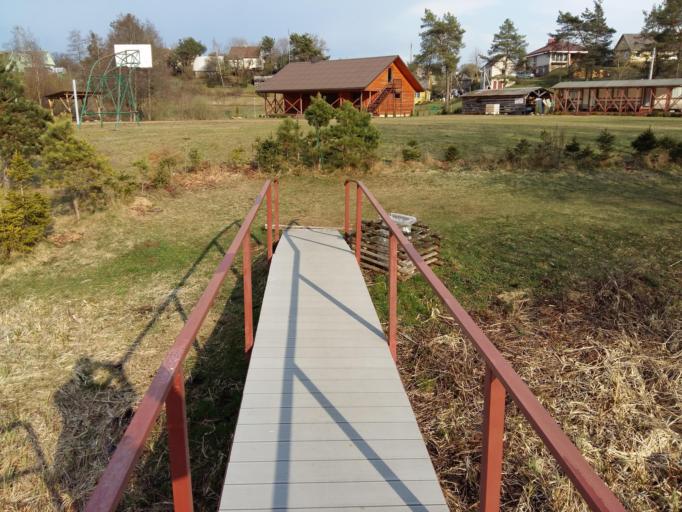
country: LT
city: Svencioneliai
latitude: 55.1566
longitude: 25.9872
